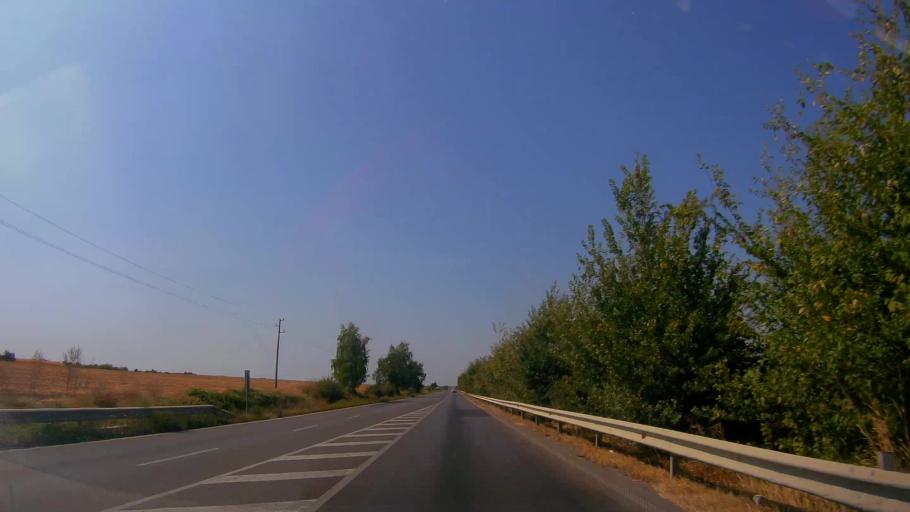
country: BG
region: Ruse
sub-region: Obshtina Vetovo
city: Senovo
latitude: 43.5619
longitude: 26.3526
